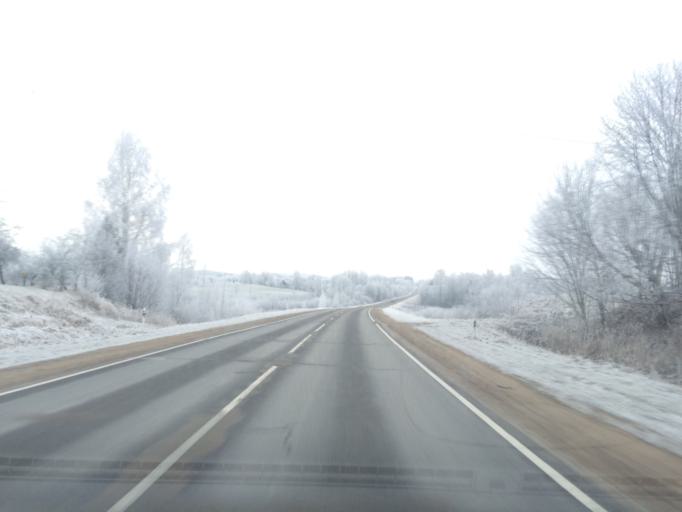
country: LV
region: Rezekne
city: Rezekne
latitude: 56.6133
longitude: 27.4462
